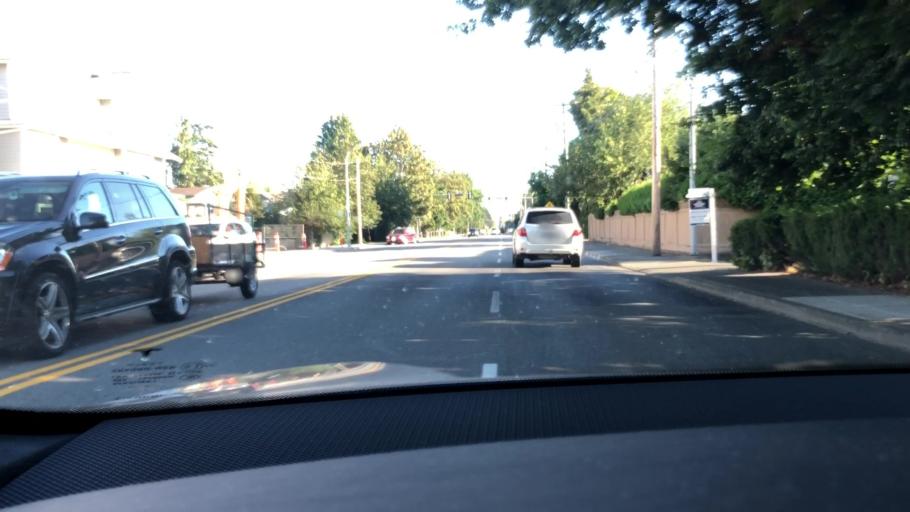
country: CA
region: British Columbia
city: Richmond
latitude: 49.1481
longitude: -123.1590
